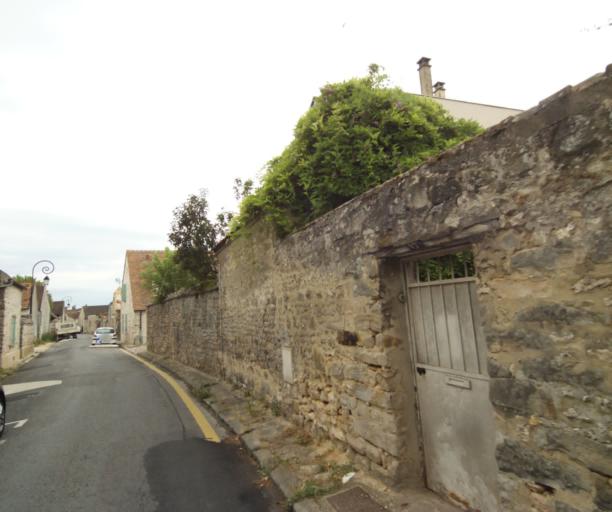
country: FR
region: Ile-de-France
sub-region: Departement de l'Essonne
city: Soisy-sur-Ecole
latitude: 48.4775
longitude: 2.4919
